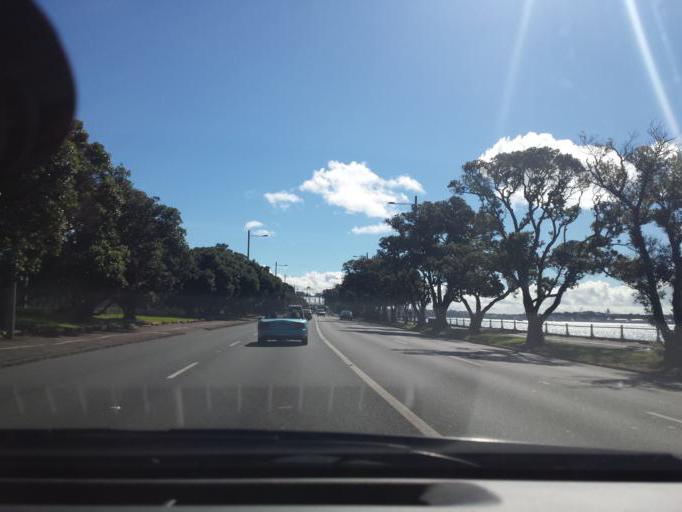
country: NZ
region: Auckland
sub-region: Auckland
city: Auckland
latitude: -36.8514
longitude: 174.7957
